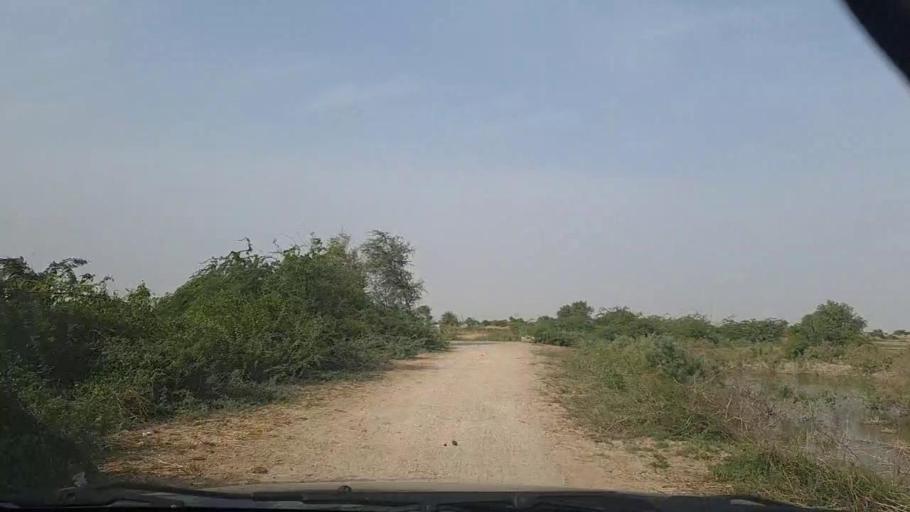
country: PK
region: Sindh
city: Thatta
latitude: 24.6169
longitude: 67.9513
